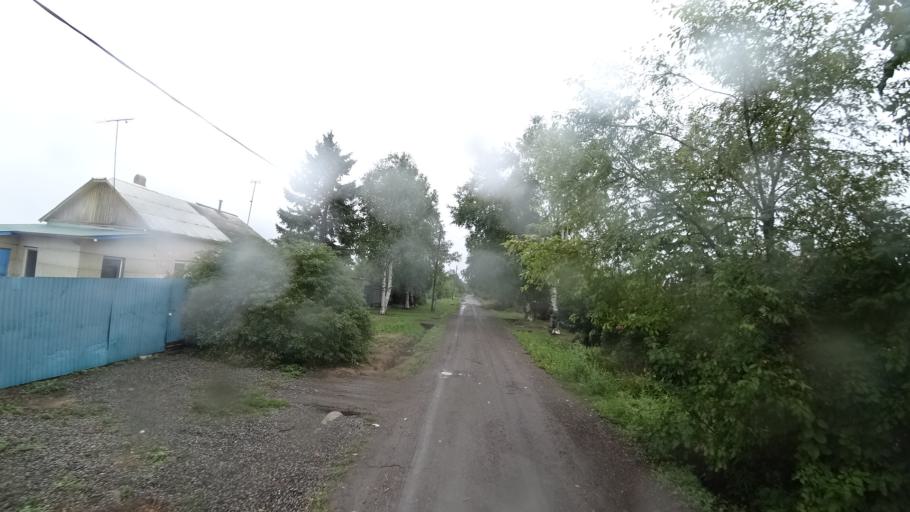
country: RU
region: Primorskiy
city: Monastyrishche
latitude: 44.2017
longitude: 132.4206
